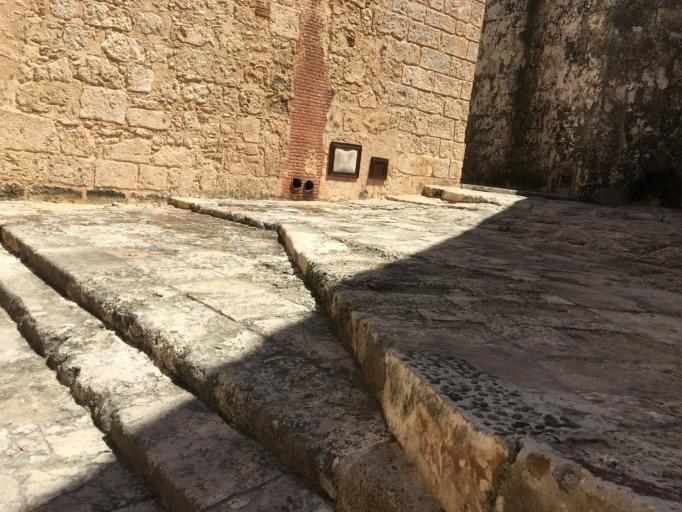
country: CU
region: La Habana
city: Centro Habana
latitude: 23.1503
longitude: -82.3570
